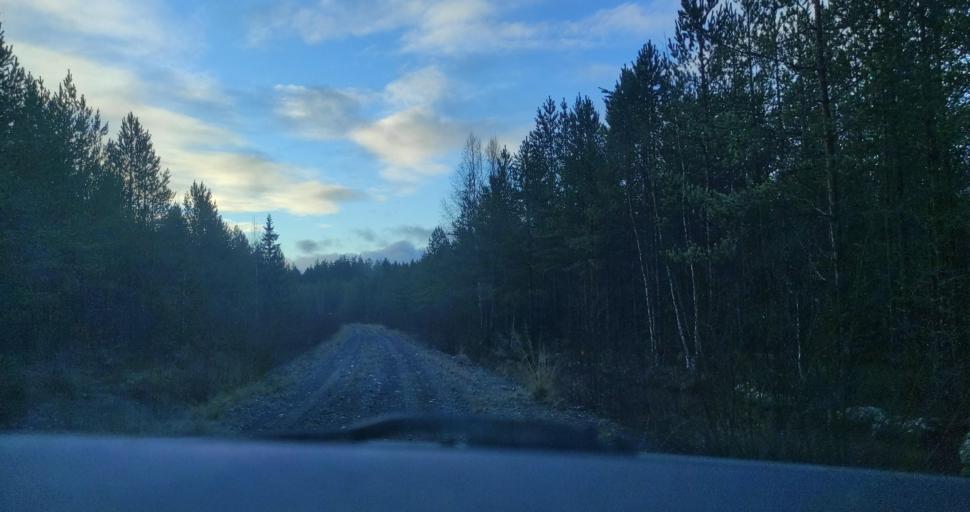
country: RU
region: Republic of Karelia
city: Pitkyaranta
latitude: 61.7377
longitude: 31.3643
